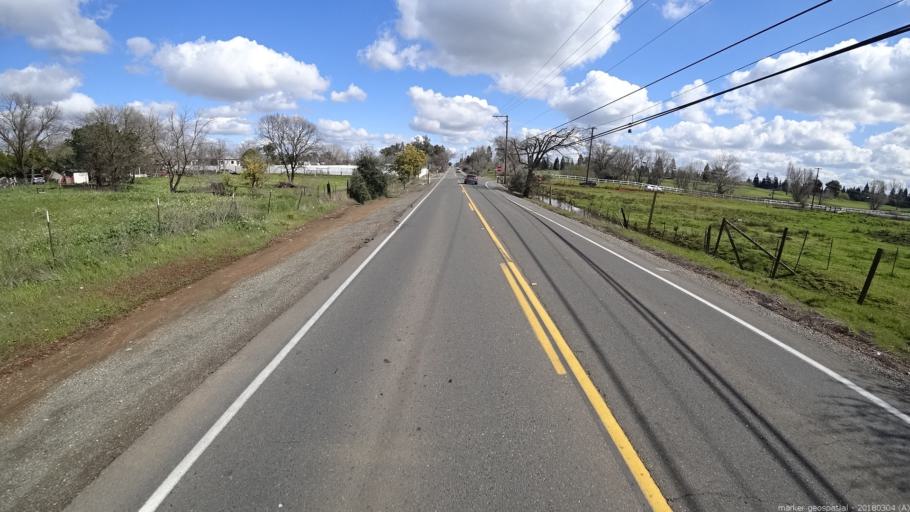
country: US
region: California
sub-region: Sacramento County
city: Vineyard
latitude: 38.4817
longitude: -121.3170
